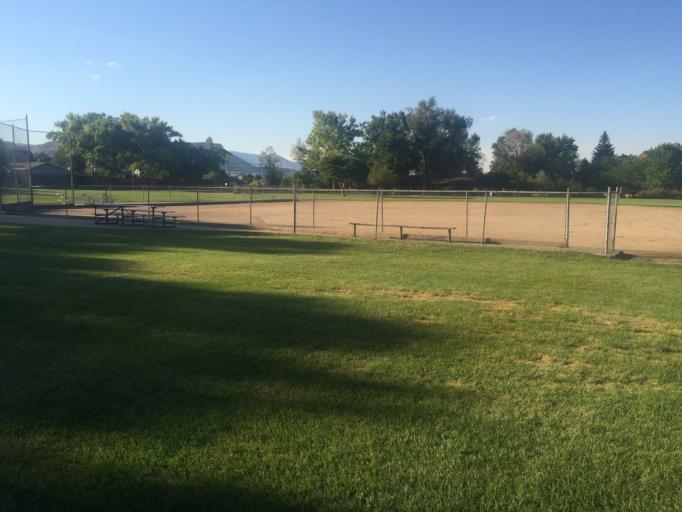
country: US
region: Colorado
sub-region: Jefferson County
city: Applewood
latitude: 39.7601
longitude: -105.1624
